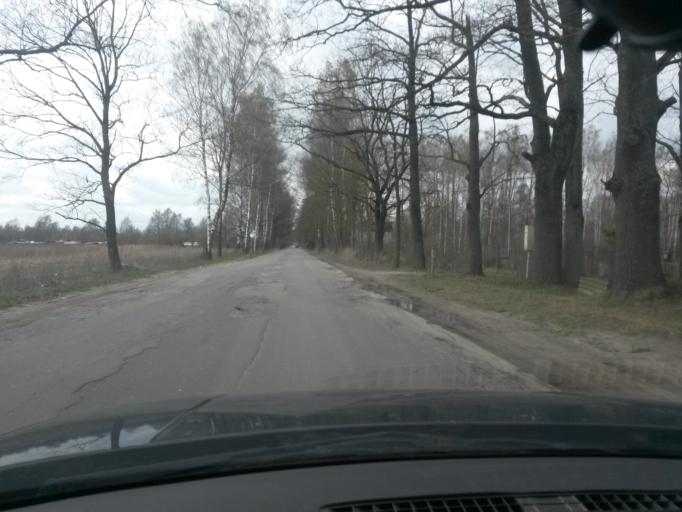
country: LV
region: Kekava
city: Kekava
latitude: 56.8926
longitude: 24.2416
